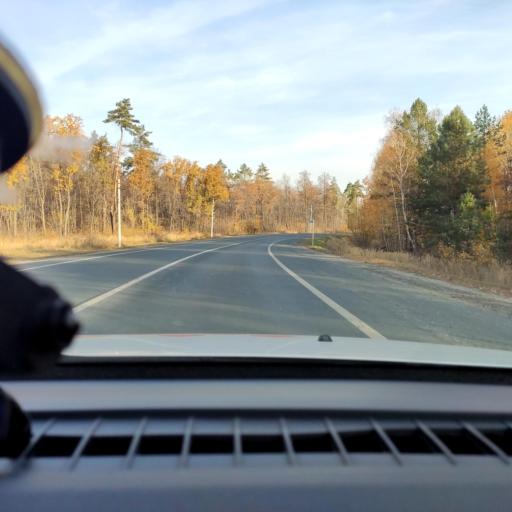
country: RU
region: Samara
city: Volzhskiy
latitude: 53.4466
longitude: 50.1227
